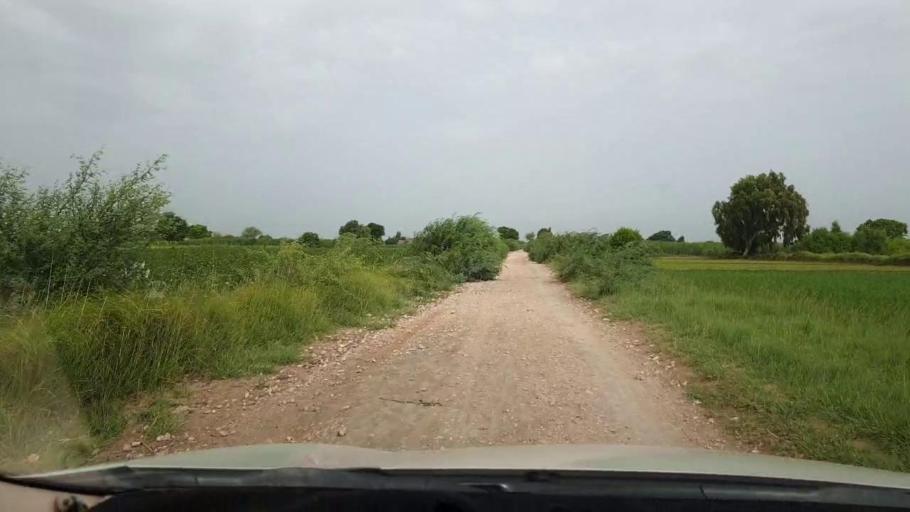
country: PK
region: Sindh
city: Matli
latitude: 25.1065
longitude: 68.6150
